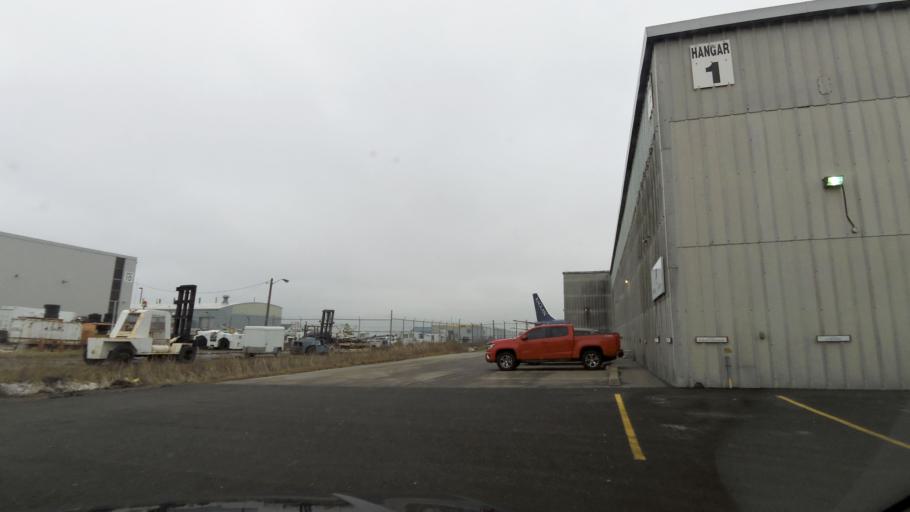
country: CA
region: Ontario
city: Etobicoke
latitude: 43.6913
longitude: -79.6485
